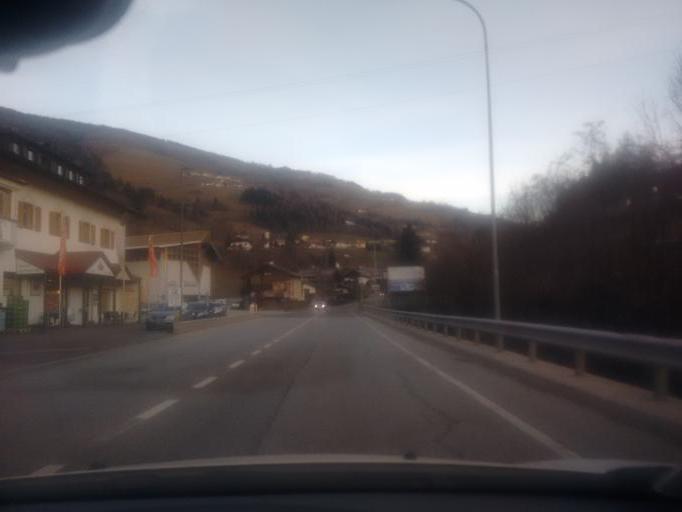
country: IT
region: Trentino-Alto Adige
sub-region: Bolzano
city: Vipiteno
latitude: 46.9035
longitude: 11.4301
